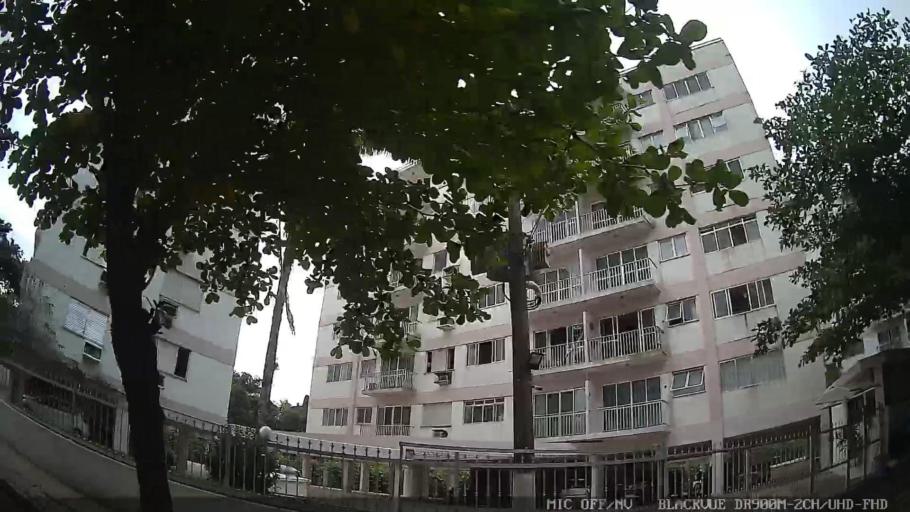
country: BR
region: Sao Paulo
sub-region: Guaruja
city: Guaruja
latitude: -23.9922
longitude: -46.1981
